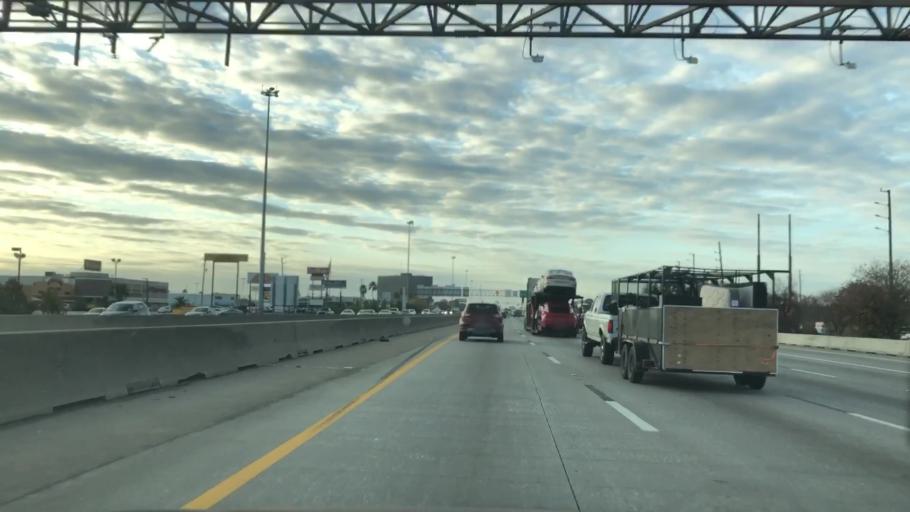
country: US
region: Texas
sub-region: Harris County
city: Aldine
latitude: 29.9294
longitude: -95.4120
